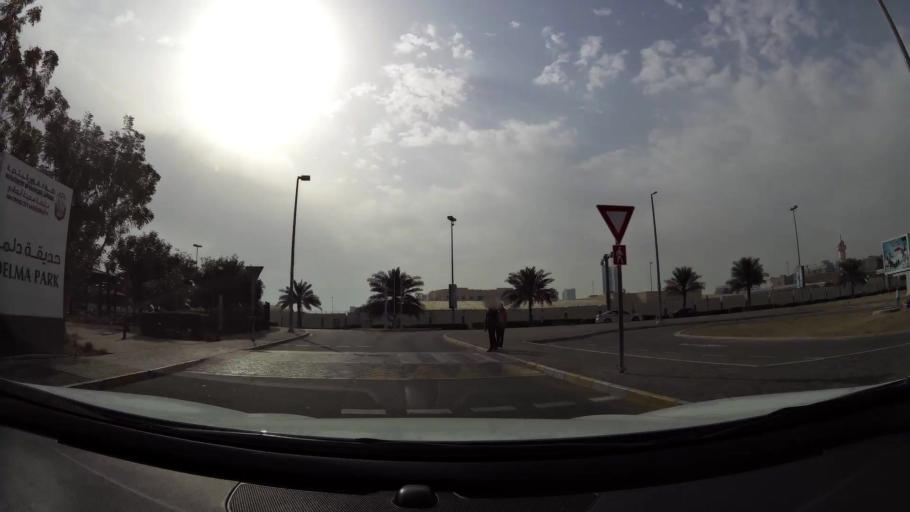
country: AE
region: Abu Dhabi
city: Abu Dhabi
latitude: 24.4727
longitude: 54.3889
